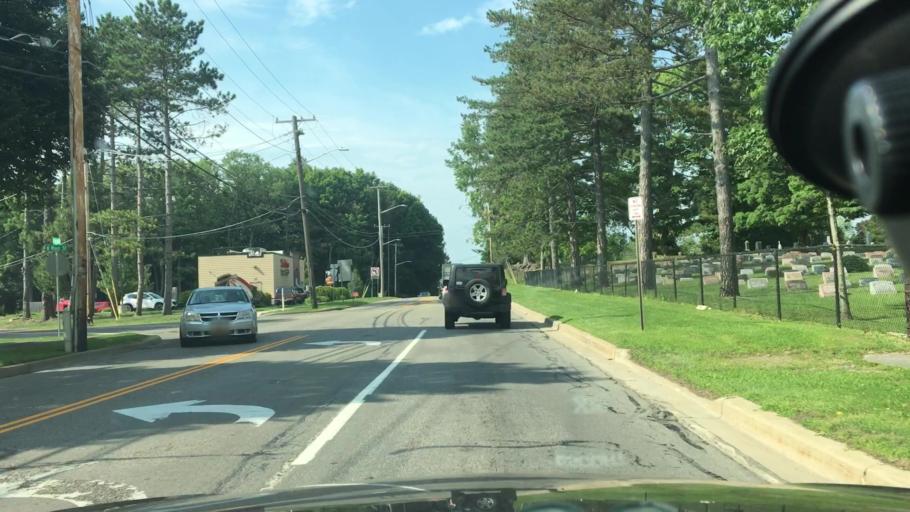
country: US
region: New York
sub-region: Chautauqua County
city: Jamestown
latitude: 42.1165
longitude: -79.2408
